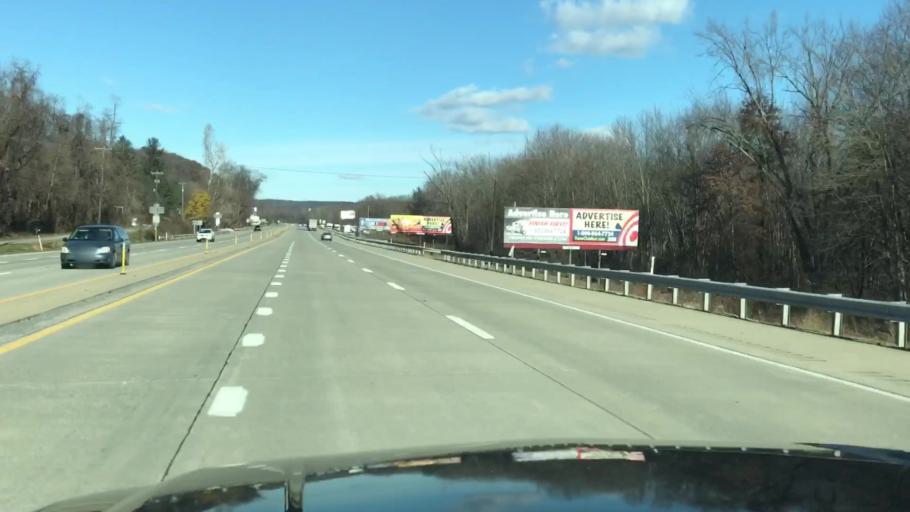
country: US
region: Pennsylvania
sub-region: Dauphin County
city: Millersburg
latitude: 40.5461
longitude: -76.9884
